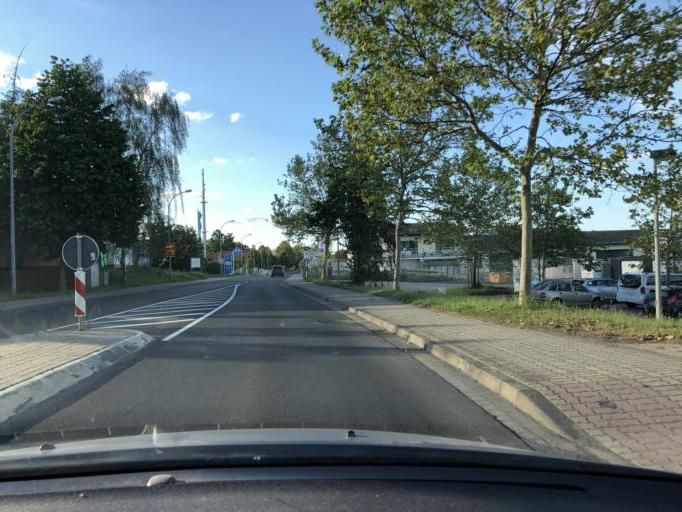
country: DE
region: Saxony
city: Groitzsch
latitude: 51.1500
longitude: 12.2872
